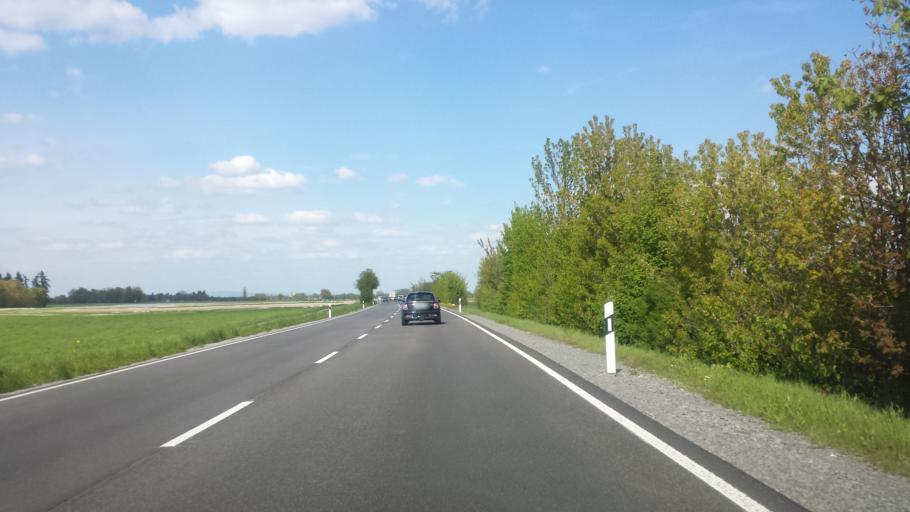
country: DE
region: Baden-Wuerttemberg
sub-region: Karlsruhe Region
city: Weingarten
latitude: 49.0822
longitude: 8.4748
